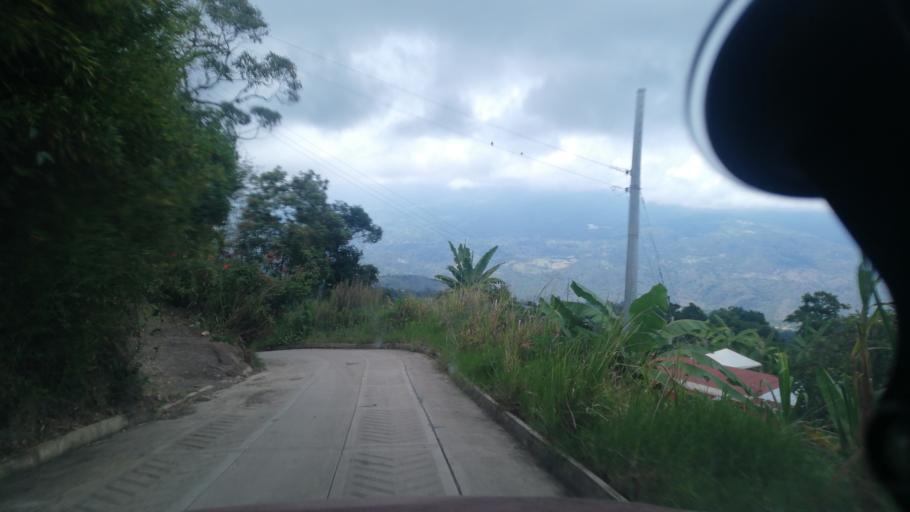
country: CO
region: Cundinamarca
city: San Antonio del Tequendama
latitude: 4.6620
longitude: -74.3985
